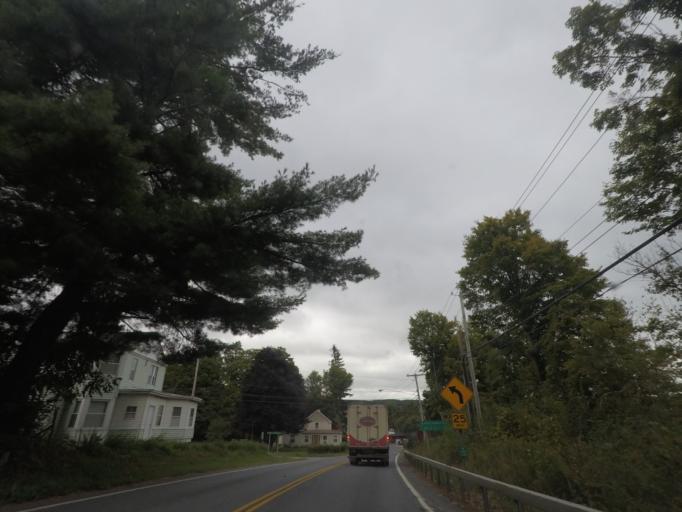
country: US
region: New York
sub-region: Rensselaer County
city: Hoosick Falls
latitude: 42.9293
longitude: -73.3438
